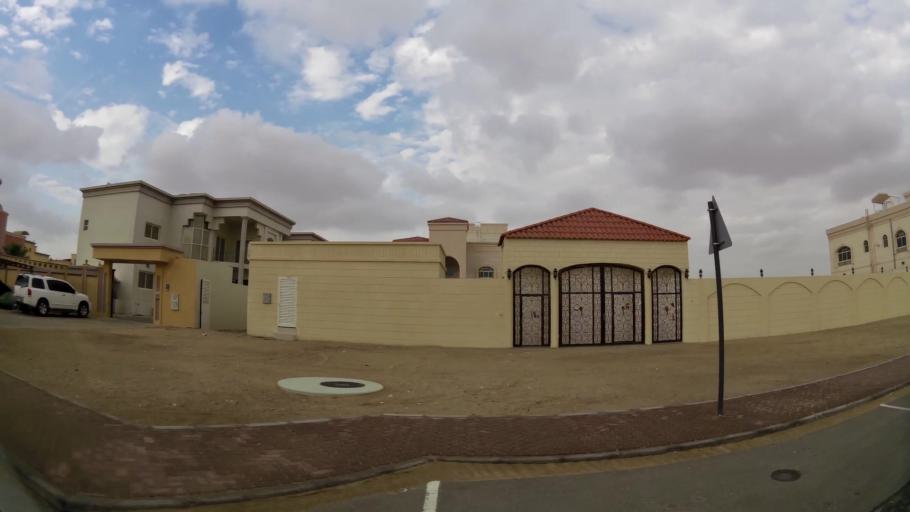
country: AE
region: Abu Dhabi
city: Abu Dhabi
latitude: 24.3531
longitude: 54.6122
